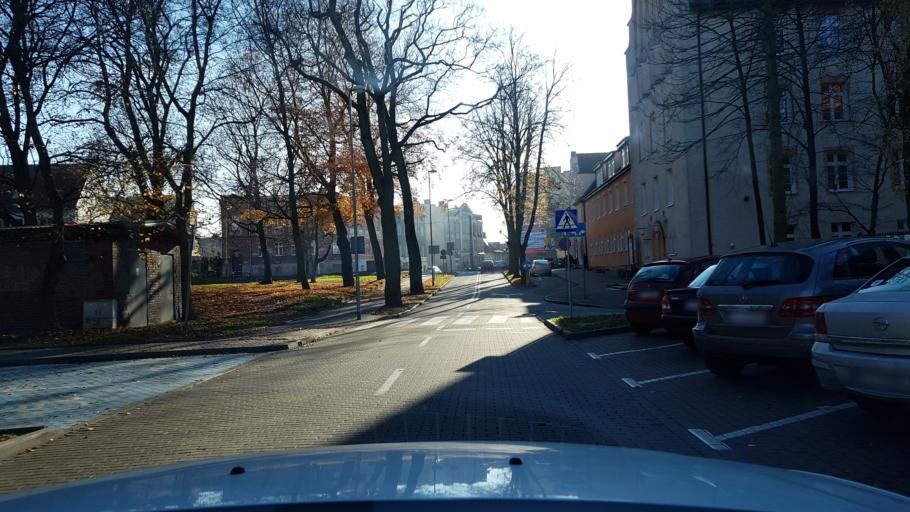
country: PL
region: West Pomeranian Voivodeship
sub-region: Powiat stargardzki
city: Stargard Szczecinski
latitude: 53.3351
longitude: 15.0385
